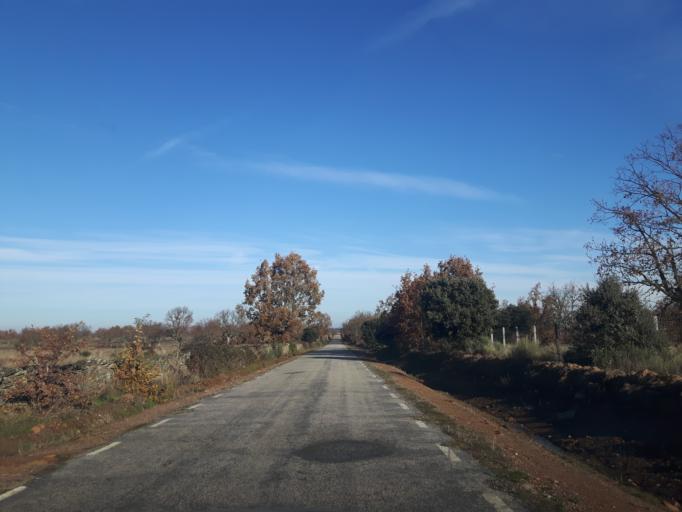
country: ES
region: Castille and Leon
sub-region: Provincia de Salamanca
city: Olmedo de Camaces
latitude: 40.9246
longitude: -6.6175
